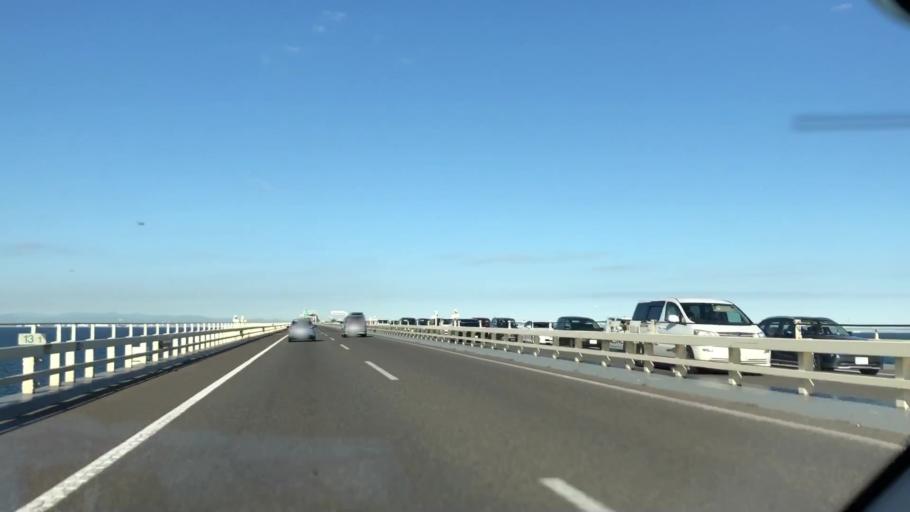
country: JP
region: Chiba
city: Kisarazu
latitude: 35.4436
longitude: 139.9047
